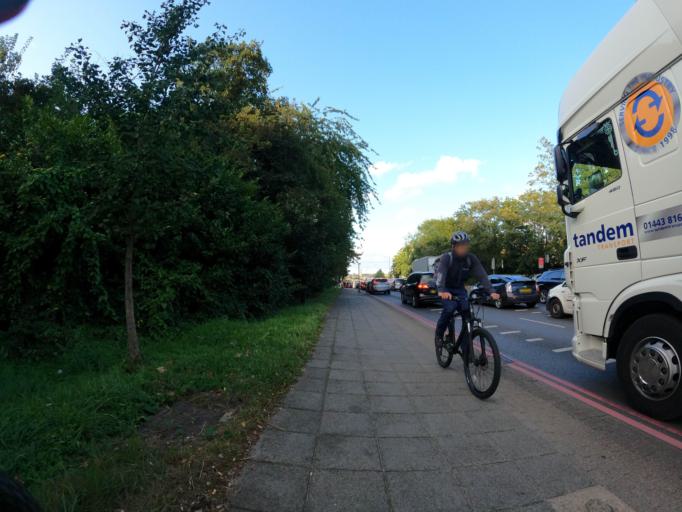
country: GB
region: England
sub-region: Greater London
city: Ealing Broadway
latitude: 51.5271
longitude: -0.2924
